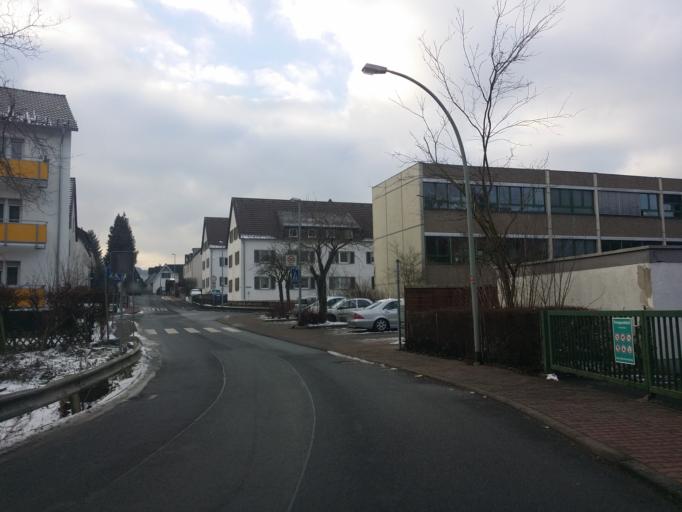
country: DE
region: Hesse
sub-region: Regierungsbezirk Darmstadt
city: Idstein
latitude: 50.2151
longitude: 8.2694
